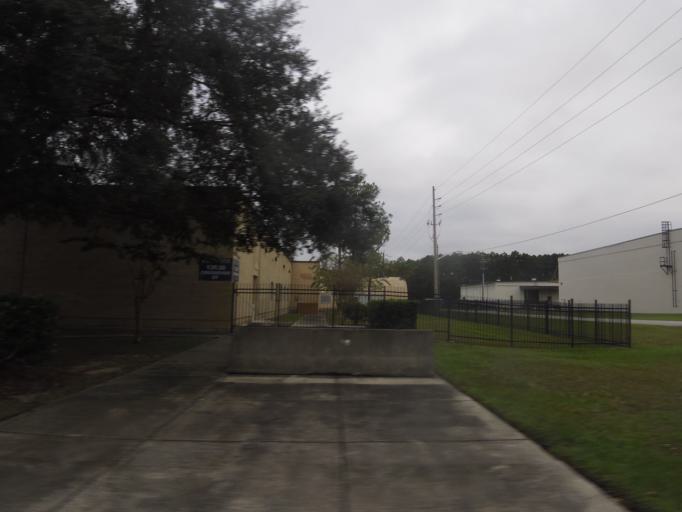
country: US
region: Florida
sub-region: Duval County
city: Baldwin
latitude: 30.2229
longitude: -81.8896
